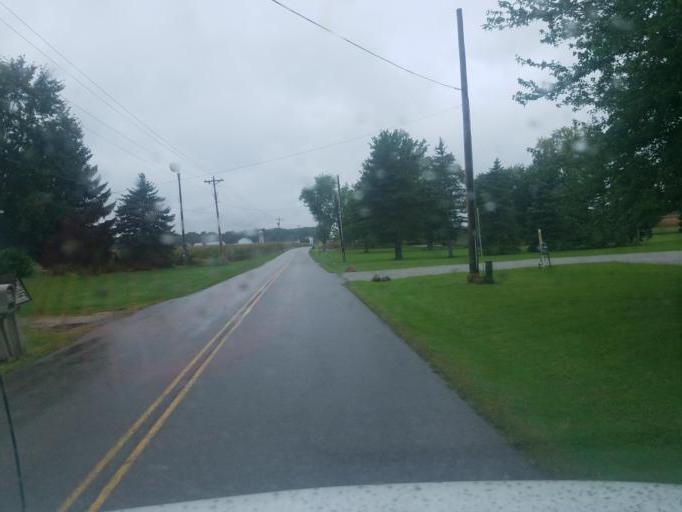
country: US
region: Ohio
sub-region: Medina County
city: Westfield Center
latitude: 40.9736
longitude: -81.9767
